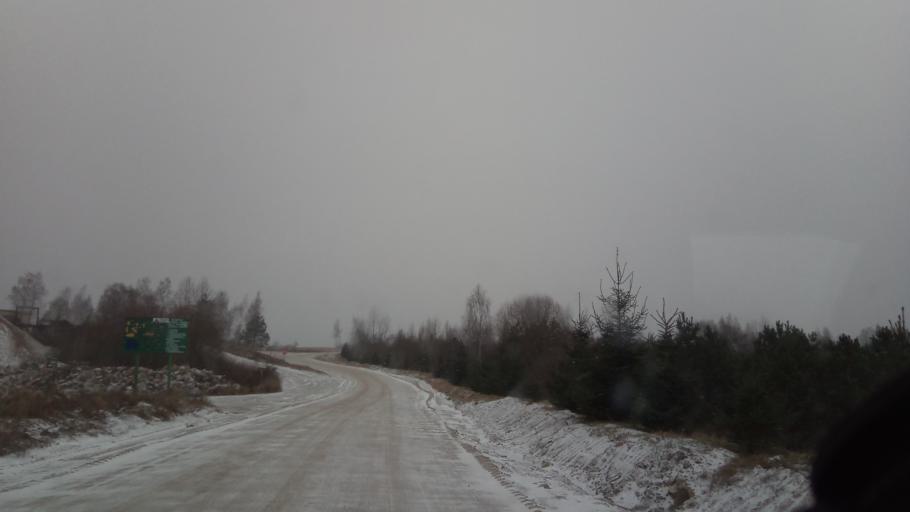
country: LT
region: Vilnius County
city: Ukmerge
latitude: 55.3310
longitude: 24.8835
